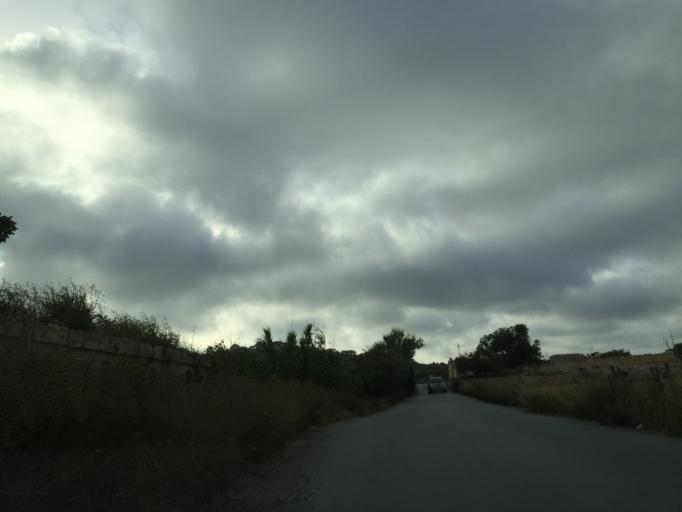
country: MT
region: Ir-Rabat
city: Rabat
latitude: 35.8687
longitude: 14.4152
